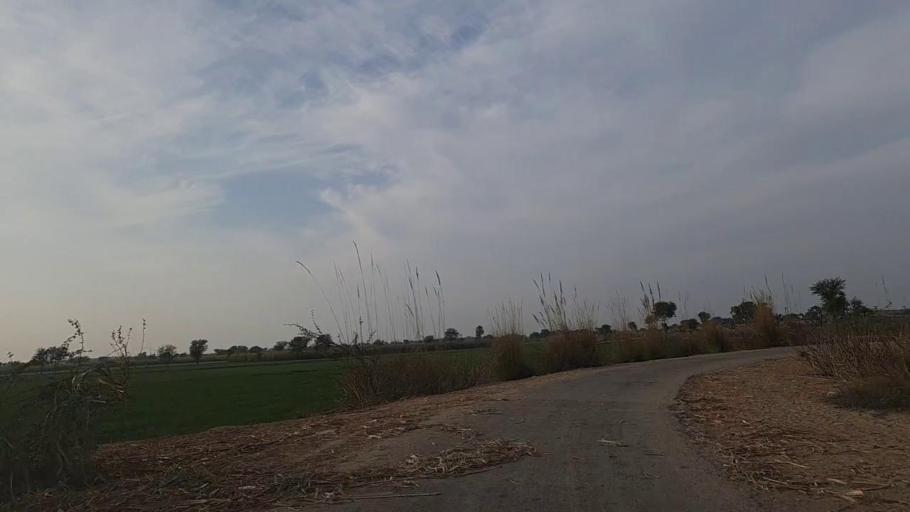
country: PK
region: Sindh
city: Daur
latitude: 26.5032
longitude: 68.4407
